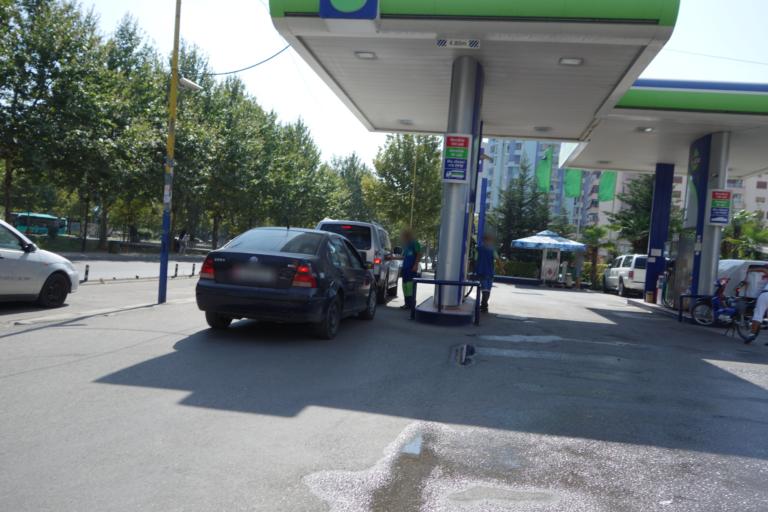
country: AL
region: Tirane
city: Tirana
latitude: 41.3229
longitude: 19.8119
